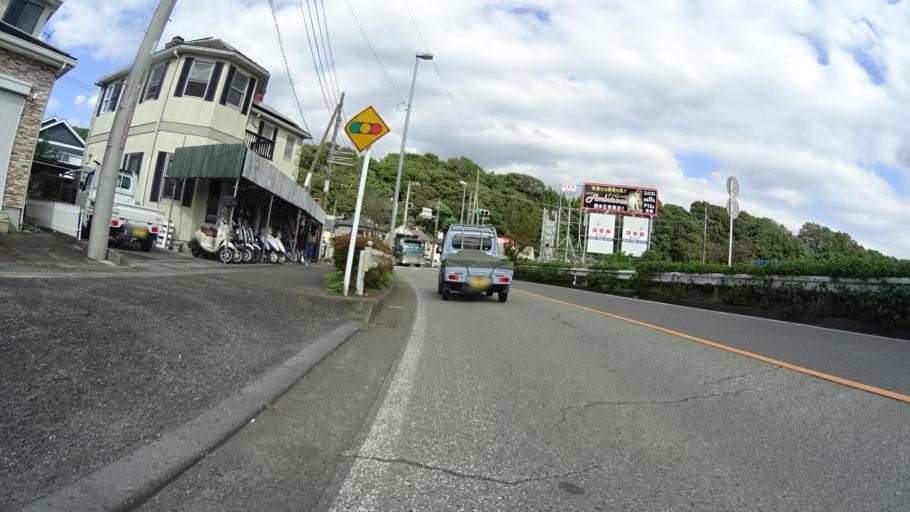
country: JP
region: Kanagawa
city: Zama
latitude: 35.5431
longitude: 139.3334
